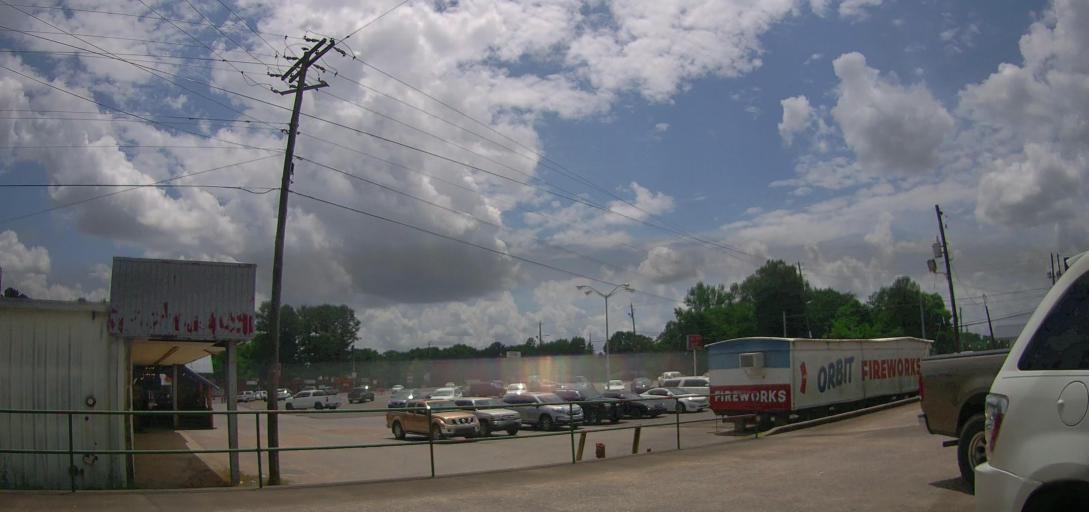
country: US
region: Alabama
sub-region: Marion County
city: Hamilton
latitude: 34.1379
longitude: -87.9890
